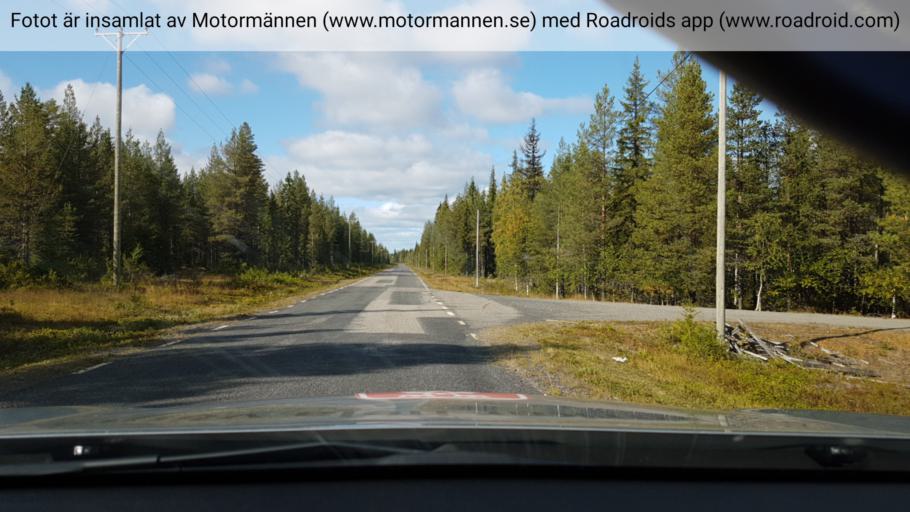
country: SE
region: Vaesterbotten
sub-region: Mala Kommun
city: Mala
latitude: 65.3609
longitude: 18.6650
